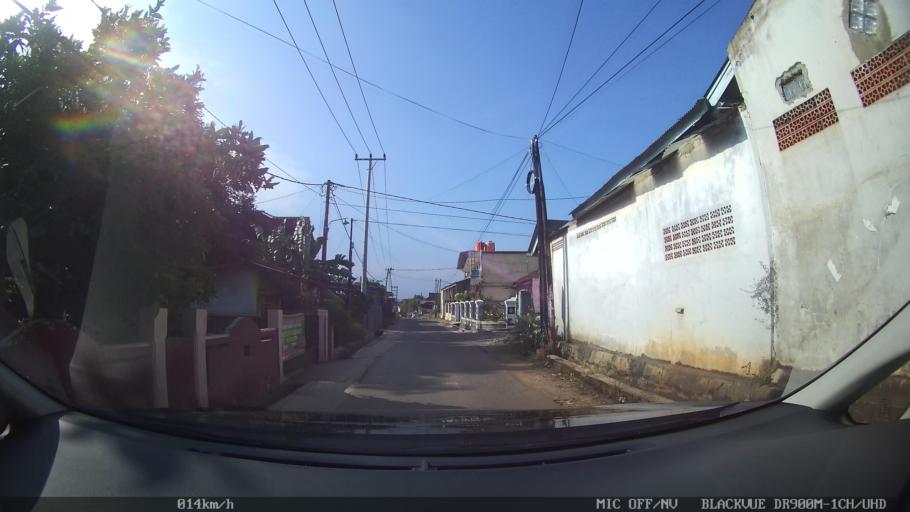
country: ID
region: Lampung
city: Kedaton
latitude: -5.3738
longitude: 105.2335
